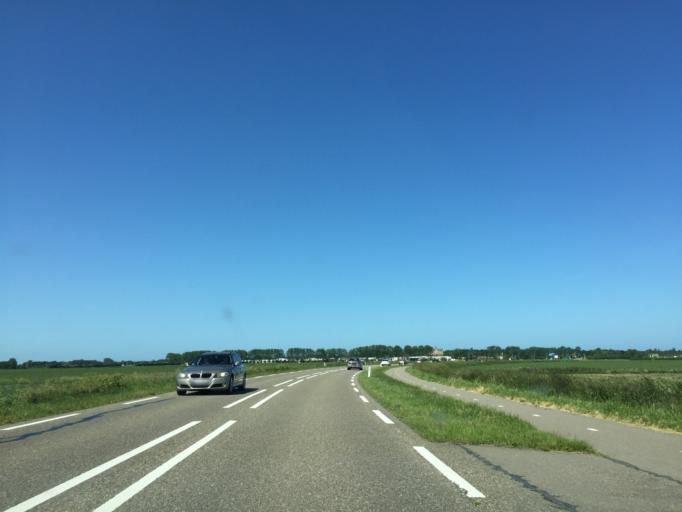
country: NL
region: Zeeland
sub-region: Schouwen-Duiveland
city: Haamstede
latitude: 51.6972
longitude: 3.7648
